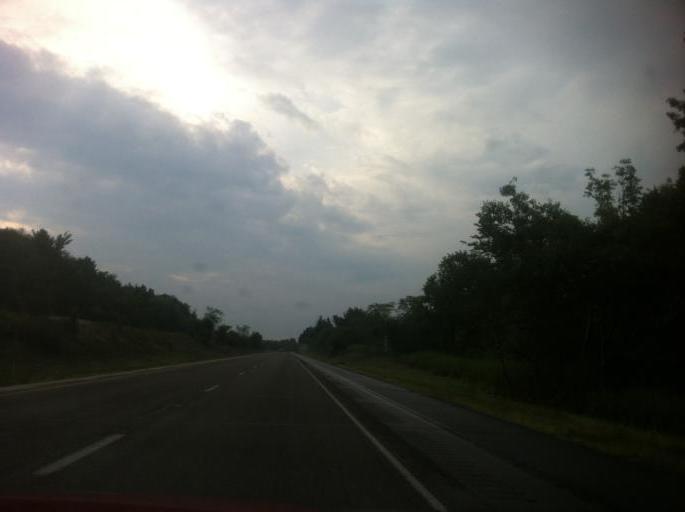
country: US
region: Pennsylvania
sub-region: Clarion County
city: Knox
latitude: 41.1931
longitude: -79.6157
